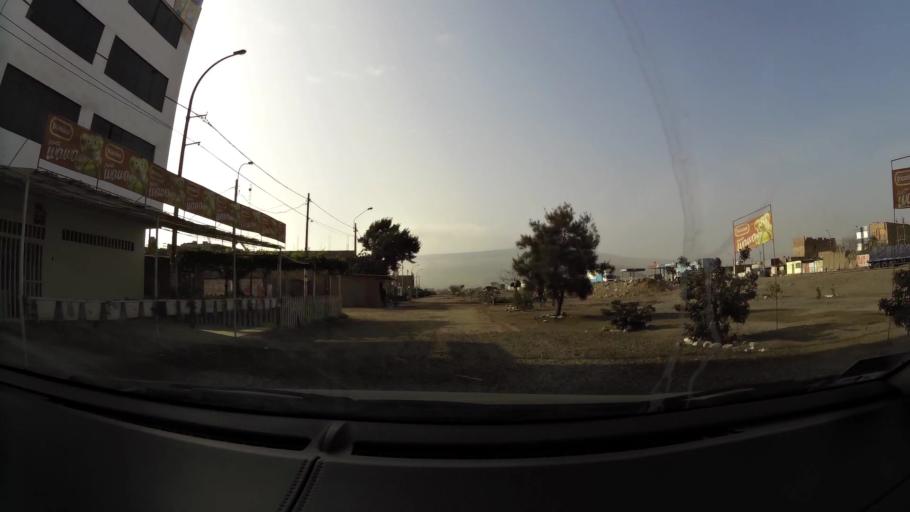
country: PE
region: Lima
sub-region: Lima
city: Santa Rosa
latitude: -11.7680
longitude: -77.1615
